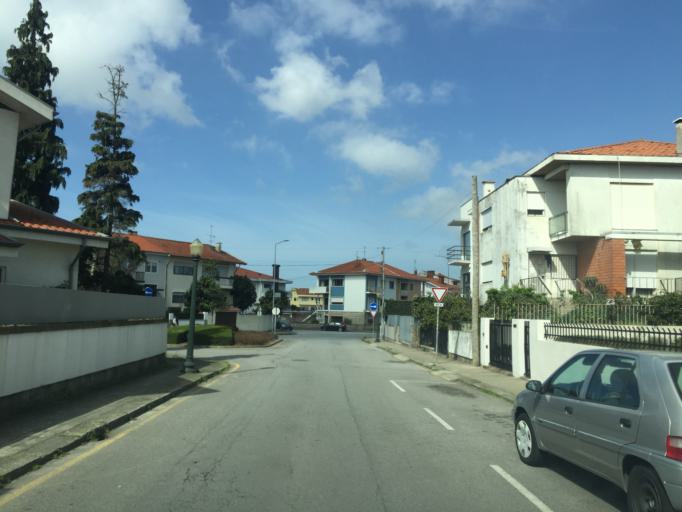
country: PT
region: Porto
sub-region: Matosinhos
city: Senhora da Hora
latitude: 41.1734
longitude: -8.6601
